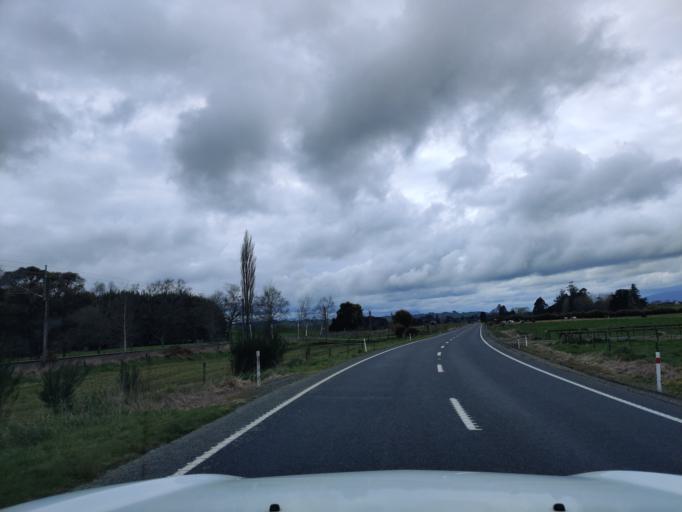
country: NZ
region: Waikato
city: Turangi
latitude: -39.0228
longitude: 175.3799
